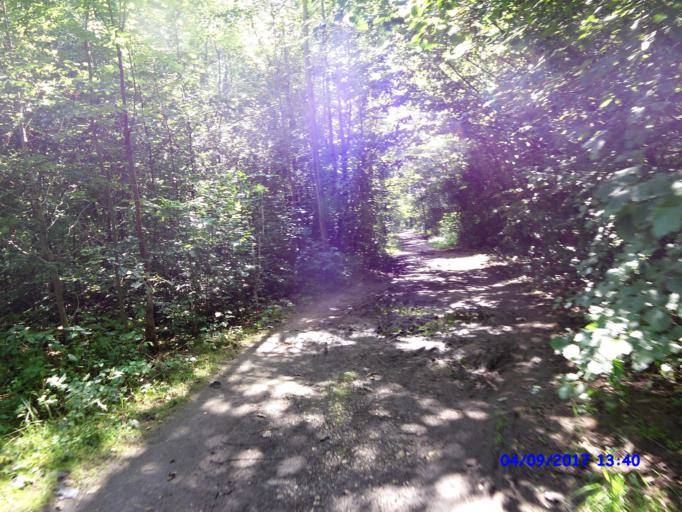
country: DE
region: Saxony
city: Taucha
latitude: 51.3552
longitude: 12.4719
